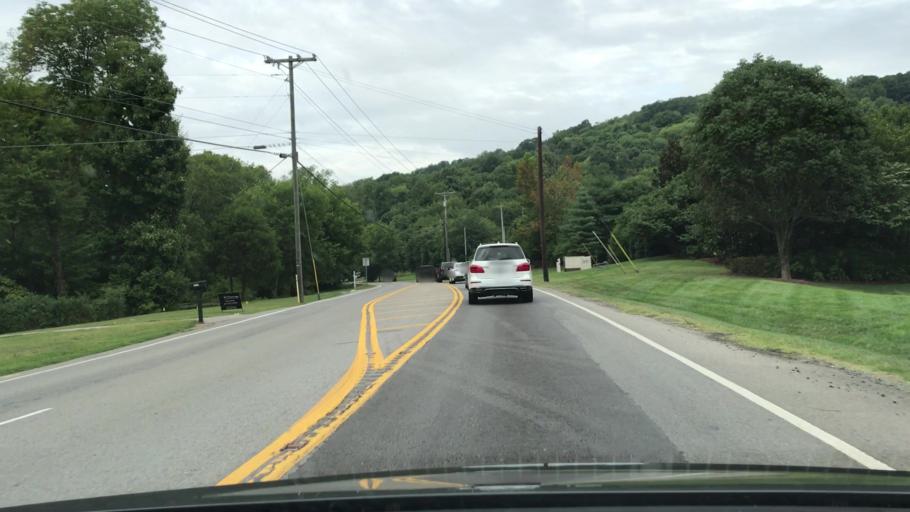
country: US
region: Tennessee
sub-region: Williamson County
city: Brentwood Estates
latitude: 35.9374
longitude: -86.7710
